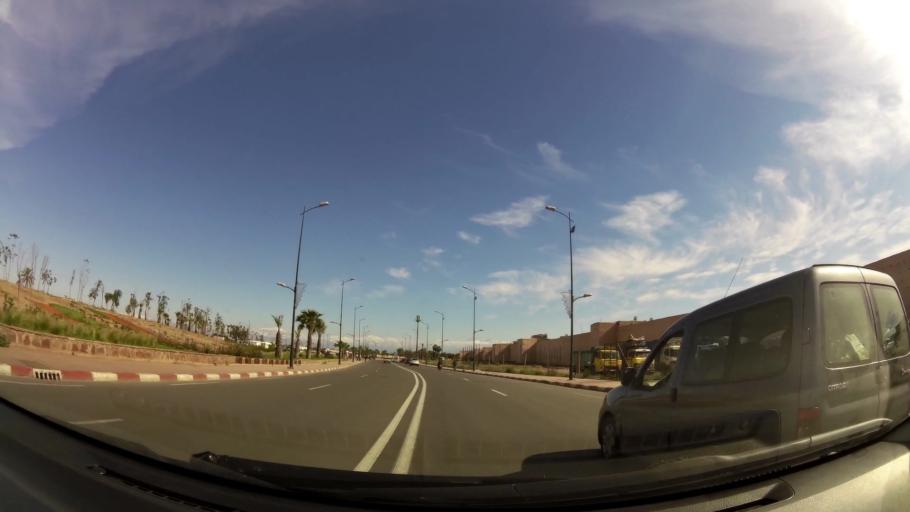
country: MA
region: Marrakech-Tensift-Al Haouz
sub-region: Marrakech
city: Marrakesh
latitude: 31.6288
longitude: -7.9724
